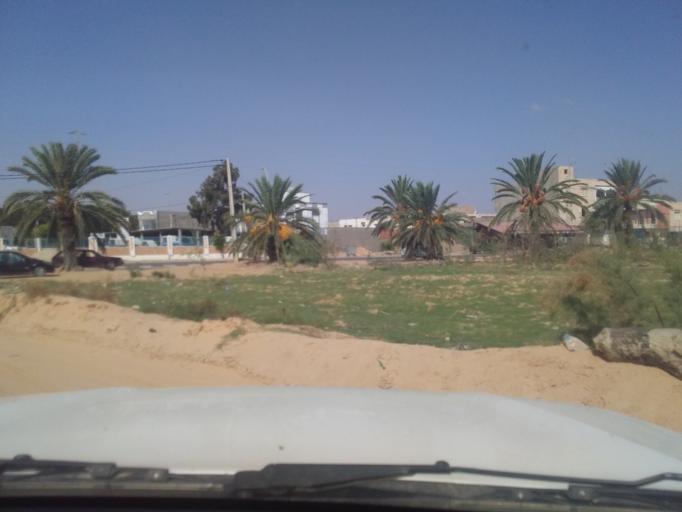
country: TN
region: Qabis
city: Gabes
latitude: 33.6279
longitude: 10.2820
